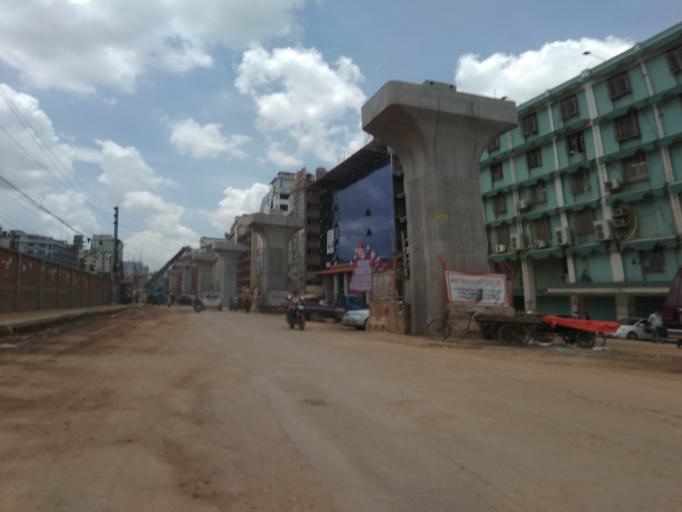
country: BD
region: Dhaka
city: Tungi
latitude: 23.8305
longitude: 90.3639
